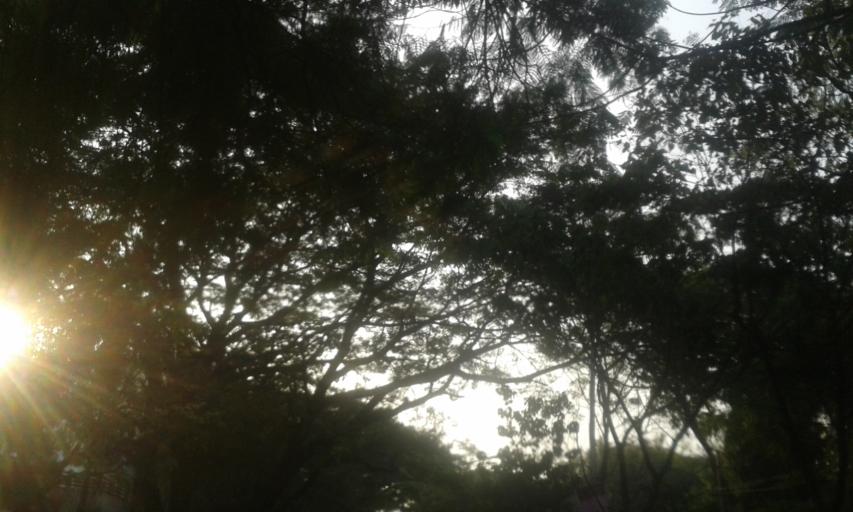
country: IN
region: Karnataka
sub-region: Bangalore Urban
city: Bangalore
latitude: 12.9063
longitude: 77.5893
